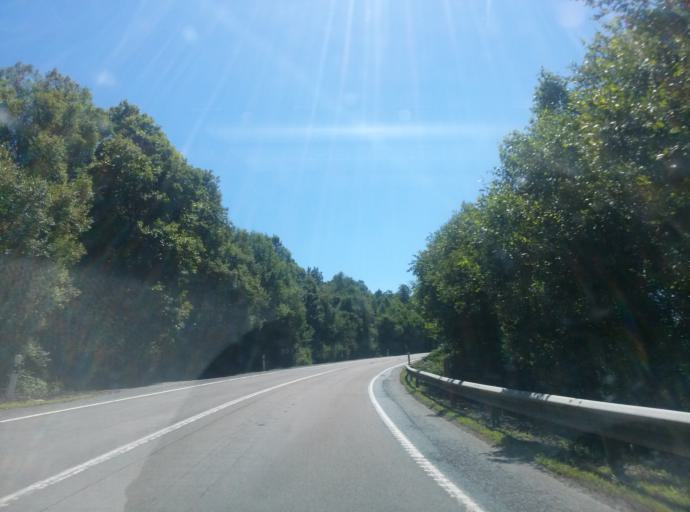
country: ES
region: Galicia
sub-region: Provincia de Lugo
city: Pol
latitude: 43.1907
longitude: -7.3394
